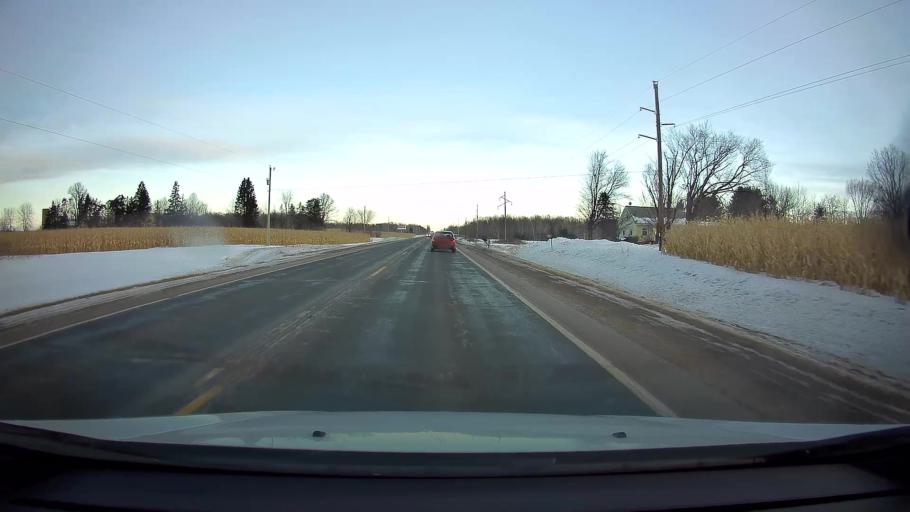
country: US
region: Wisconsin
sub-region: Barron County
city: Turtle Lake
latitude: 45.3519
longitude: -92.1669
